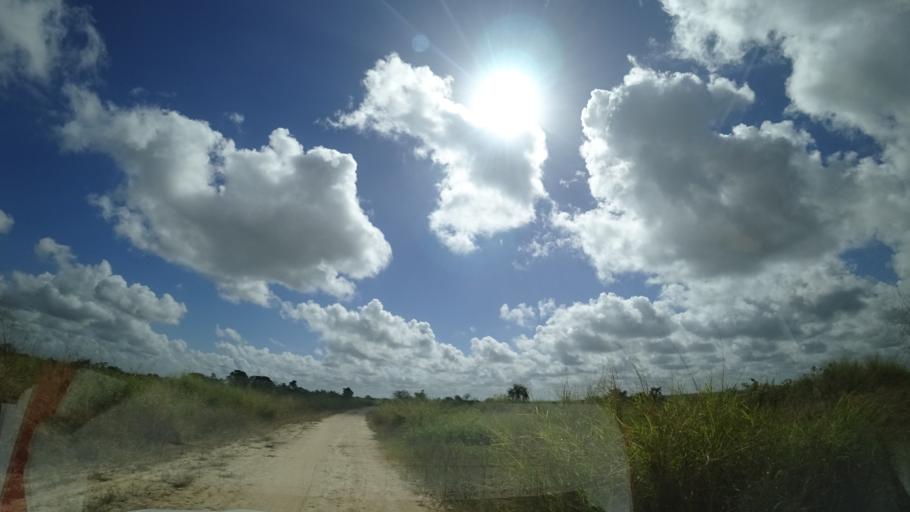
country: MZ
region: Sofala
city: Dondo
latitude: -19.4186
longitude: 34.5650
